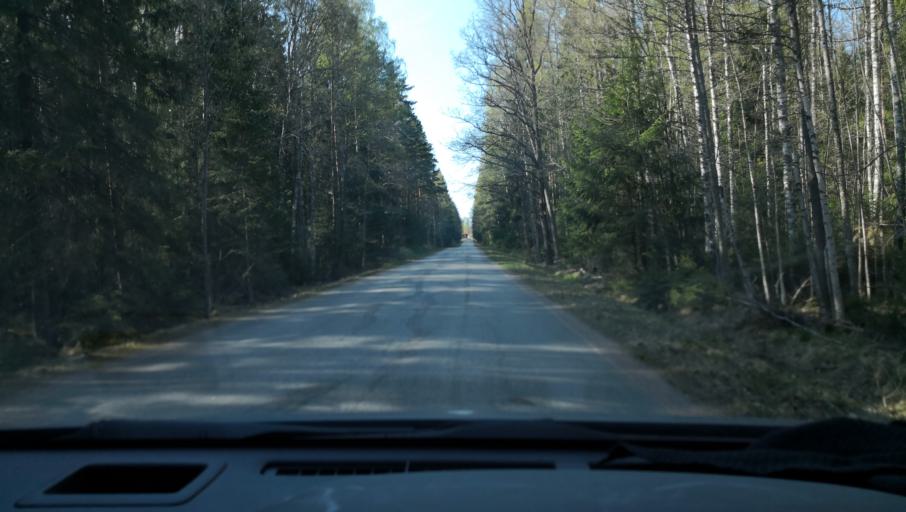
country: SE
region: Uppsala
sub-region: Heby Kommun
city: Tarnsjo
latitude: 60.2786
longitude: 16.8913
